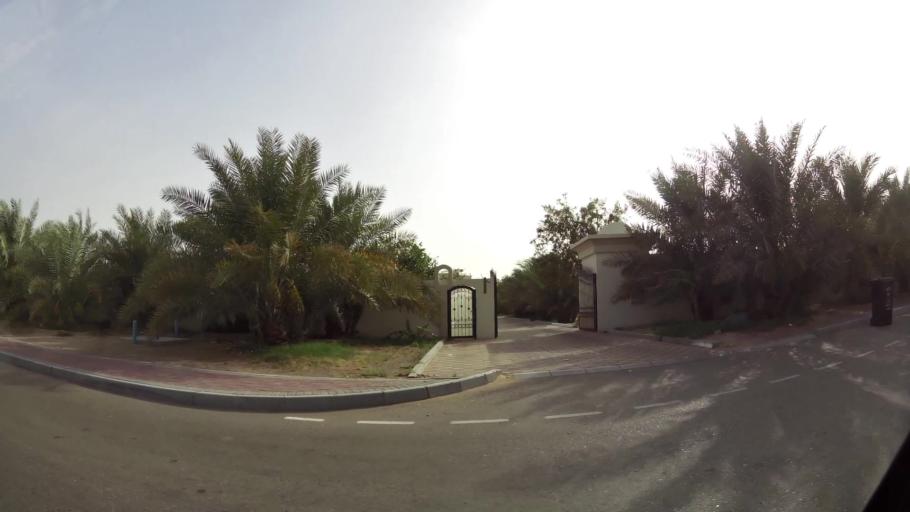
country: AE
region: Abu Dhabi
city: Al Ain
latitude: 24.2073
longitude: 55.6325
